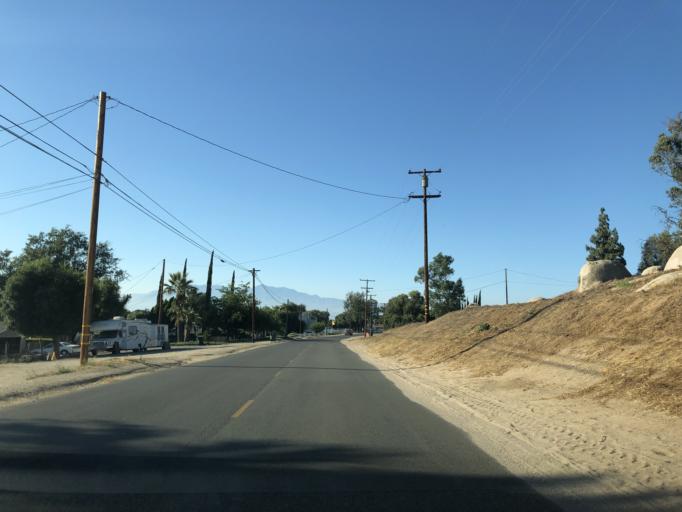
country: US
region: California
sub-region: Riverside County
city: Norco
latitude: 33.9137
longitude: -117.5442
